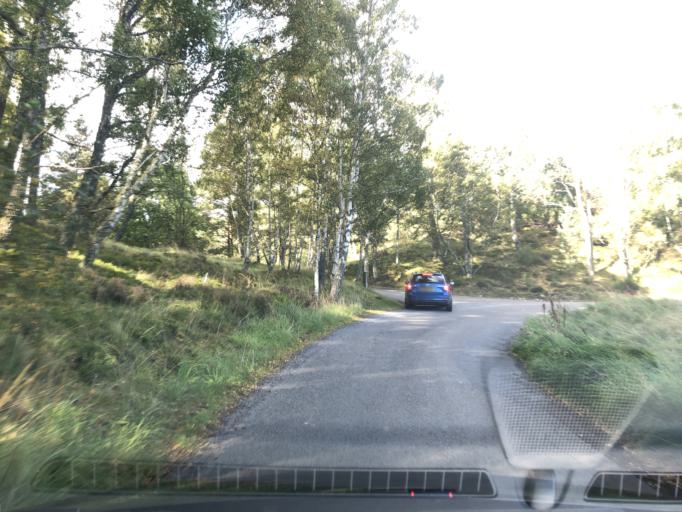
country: GB
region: Scotland
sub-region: Highland
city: Aviemore
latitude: 57.1108
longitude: -3.8906
